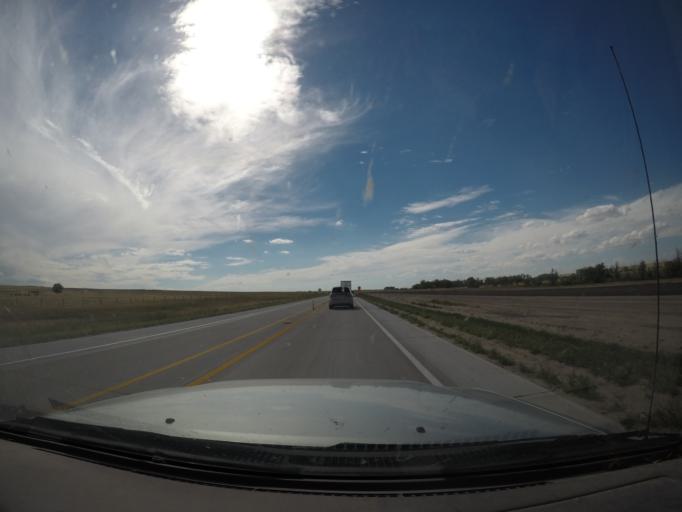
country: US
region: Nebraska
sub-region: Deuel County
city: Chappell
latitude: 41.0853
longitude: -102.4917
